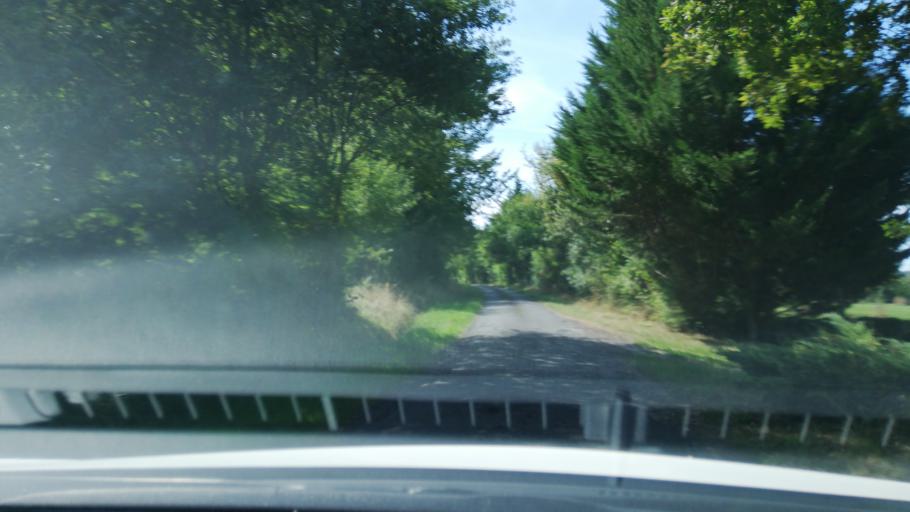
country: FR
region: Centre
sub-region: Departement d'Indre-et-Loire
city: Mazieres-de-Touraine
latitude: 47.3963
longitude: 0.4492
